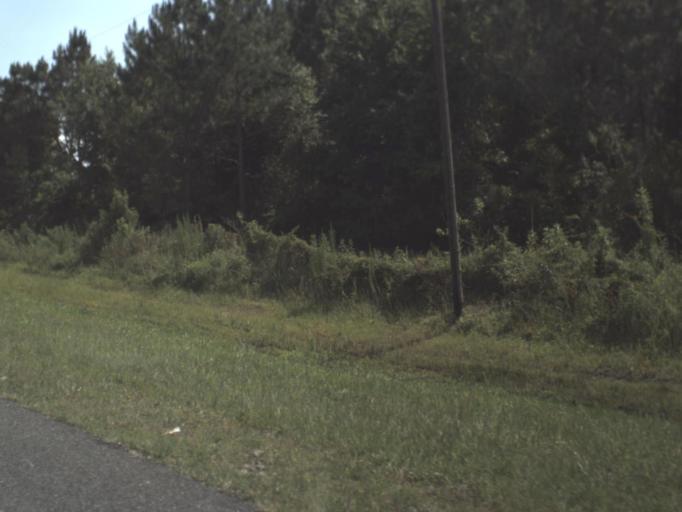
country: US
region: Florida
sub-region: Alachua County
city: Waldo
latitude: 29.7385
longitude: -82.1413
